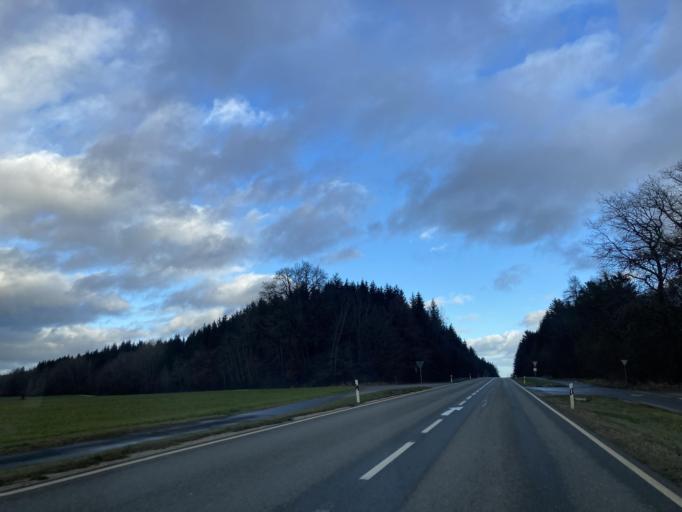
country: DE
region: Baden-Wuerttemberg
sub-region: Freiburg Region
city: Buchheim
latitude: 47.9802
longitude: 8.9703
